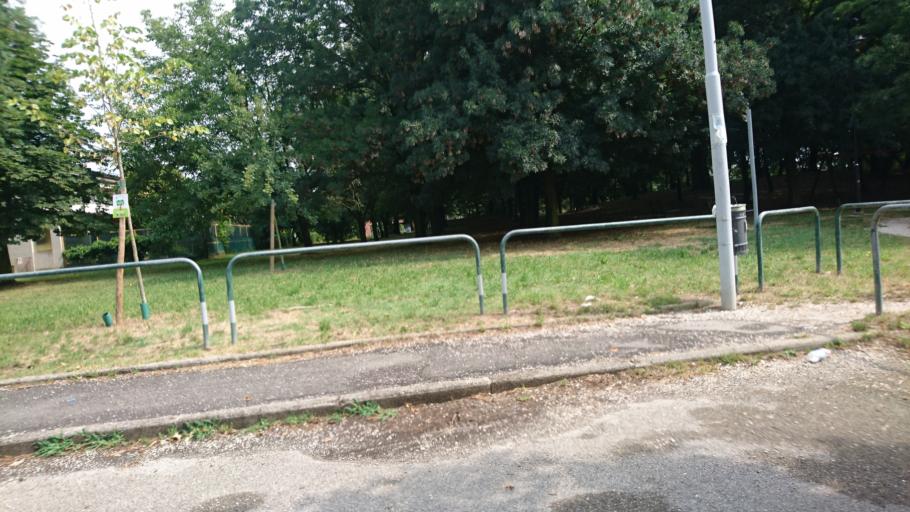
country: IT
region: Veneto
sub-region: Provincia di Padova
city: Padova
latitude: 45.3996
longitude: 11.9142
